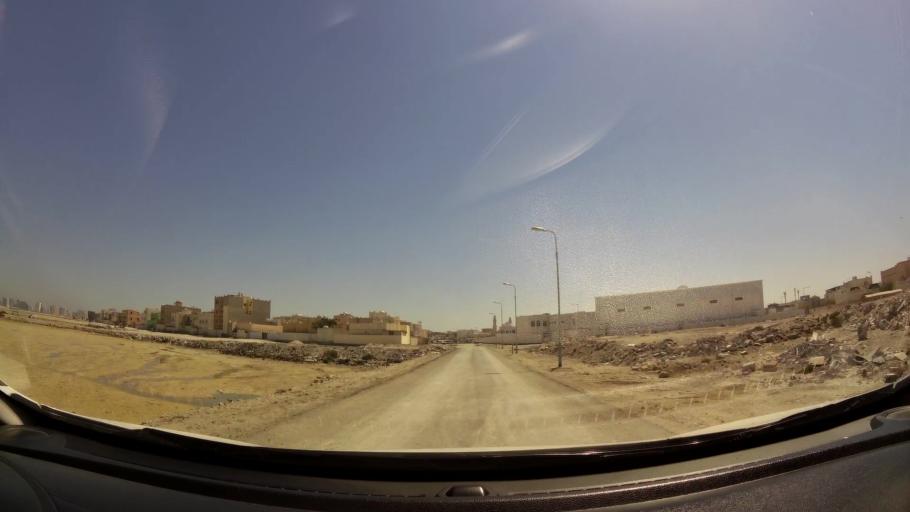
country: BH
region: Muharraq
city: Al Muharraq
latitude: 26.2889
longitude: 50.6250
